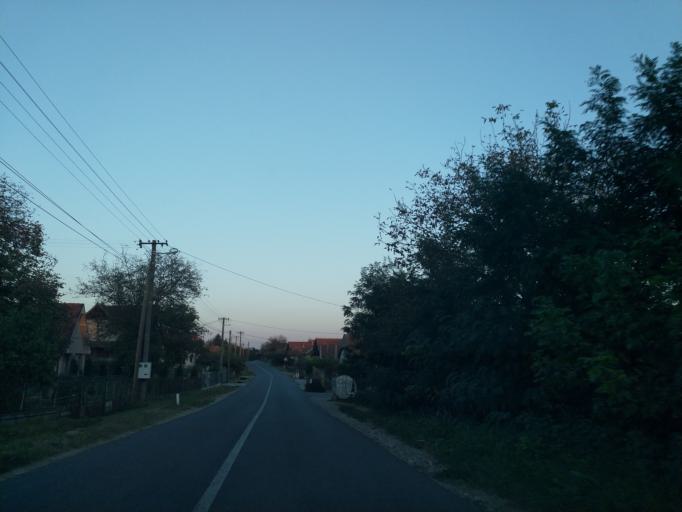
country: RS
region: Central Serbia
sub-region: Rasinski Okrug
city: Krusevac
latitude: 43.6018
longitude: 21.2560
